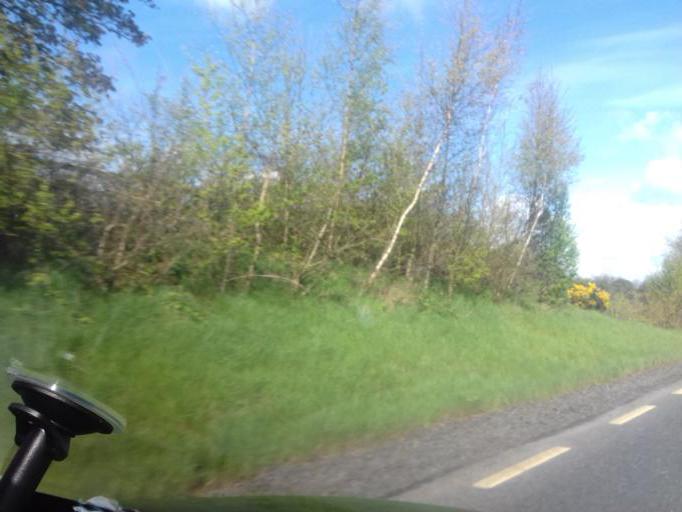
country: IE
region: Ulster
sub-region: An Cabhan
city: Mullagh
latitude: 53.7493
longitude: -6.9798
